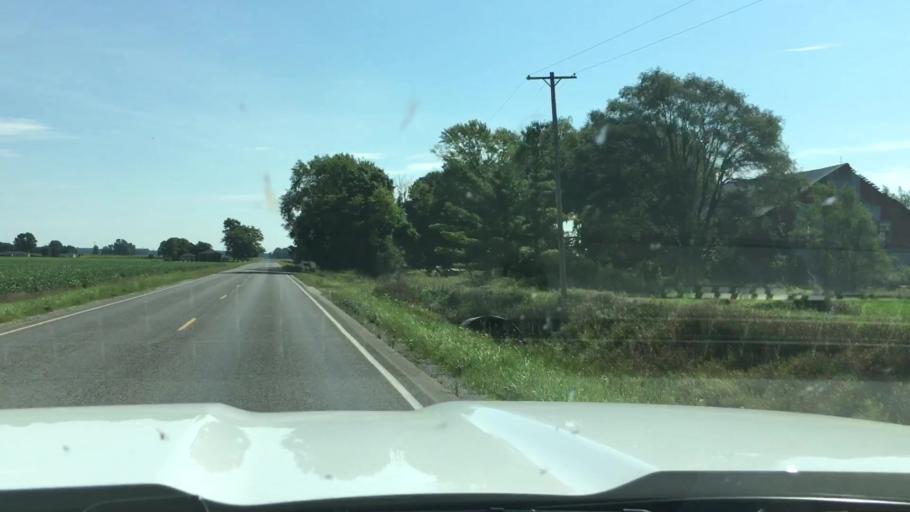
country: US
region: Michigan
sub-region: Saginaw County
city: Freeland
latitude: 43.5252
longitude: -84.2175
